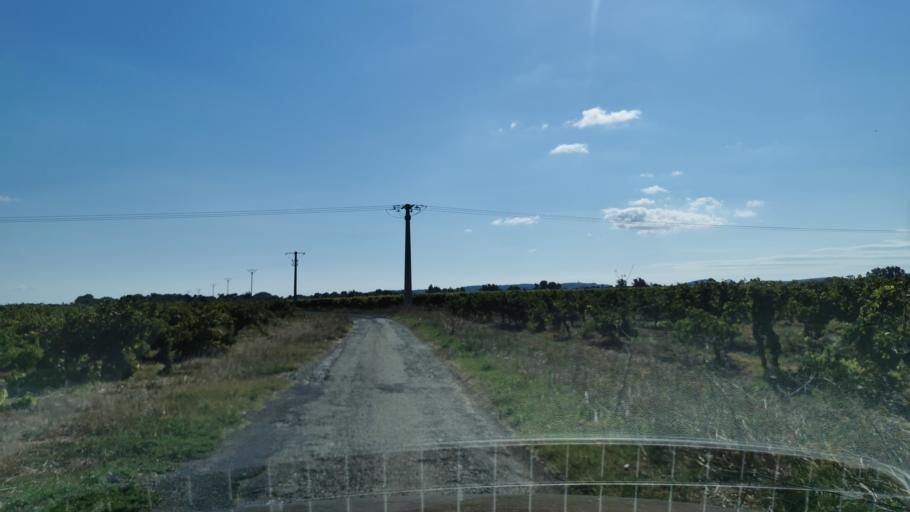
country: FR
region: Languedoc-Roussillon
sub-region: Departement de l'Aude
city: Ginestas
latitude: 43.2418
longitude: 2.8685
